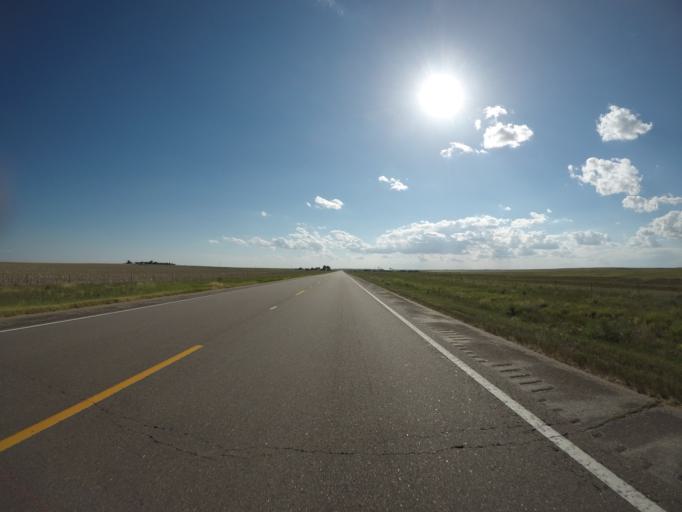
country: US
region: Colorado
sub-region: Morgan County
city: Fort Morgan
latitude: 40.6008
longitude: -103.8650
